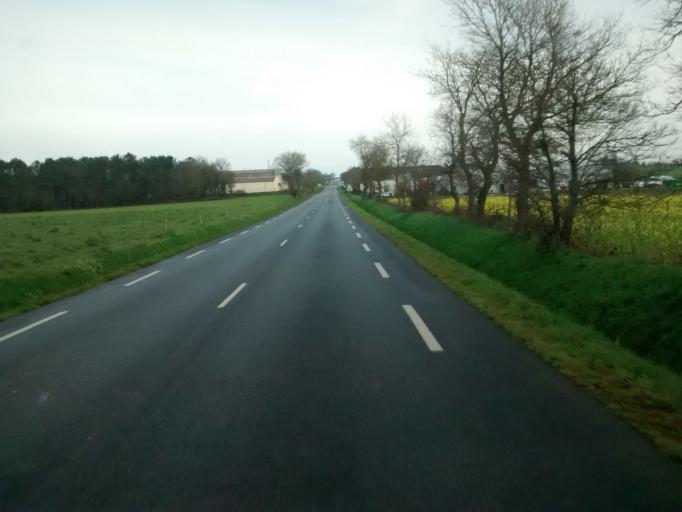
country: FR
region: Brittany
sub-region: Departement du Morbihan
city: Malestroit
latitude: 47.8452
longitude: -2.4162
